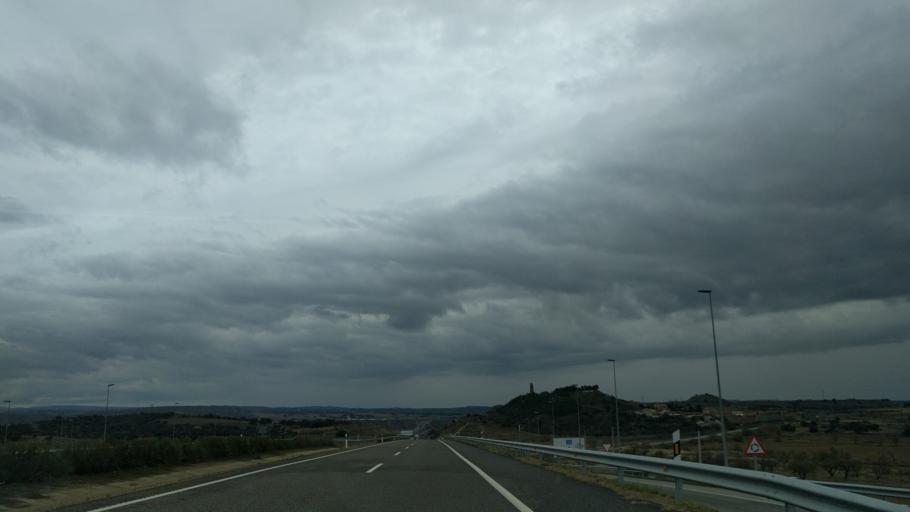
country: ES
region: Aragon
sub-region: Provincia de Huesca
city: Castejon del Puente
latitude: 41.9716
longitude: 0.1486
